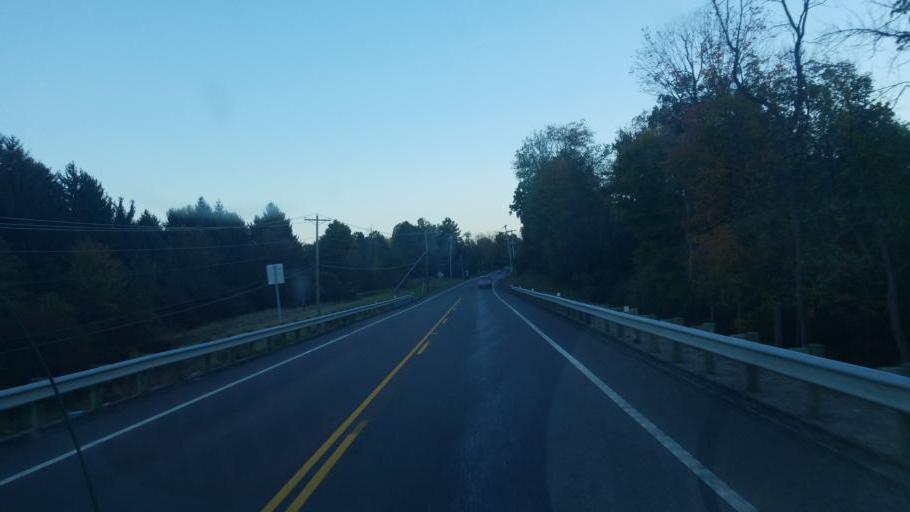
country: US
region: Ohio
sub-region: Licking County
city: Newark
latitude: 40.0321
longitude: -82.4026
